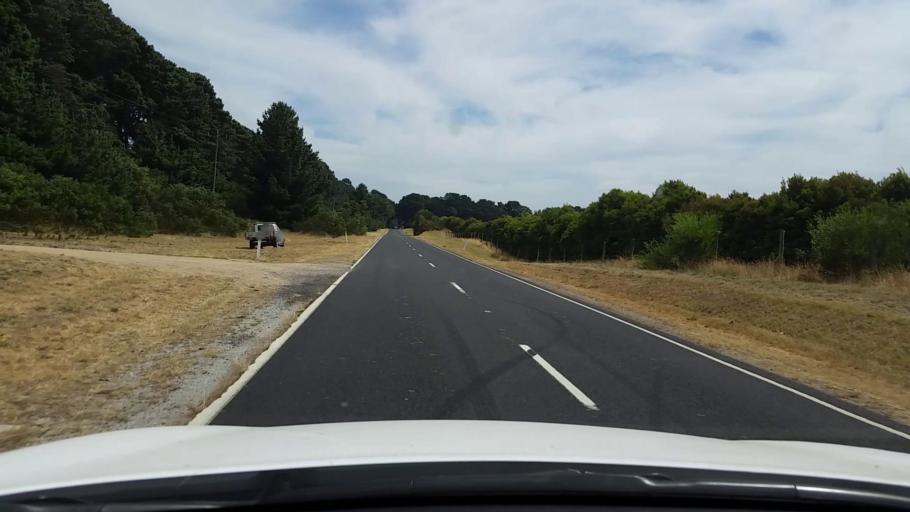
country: AU
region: Victoria
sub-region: Mornington Peninsula
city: Saint Andrews Beach
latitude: -38.4640
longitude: 144.9107
